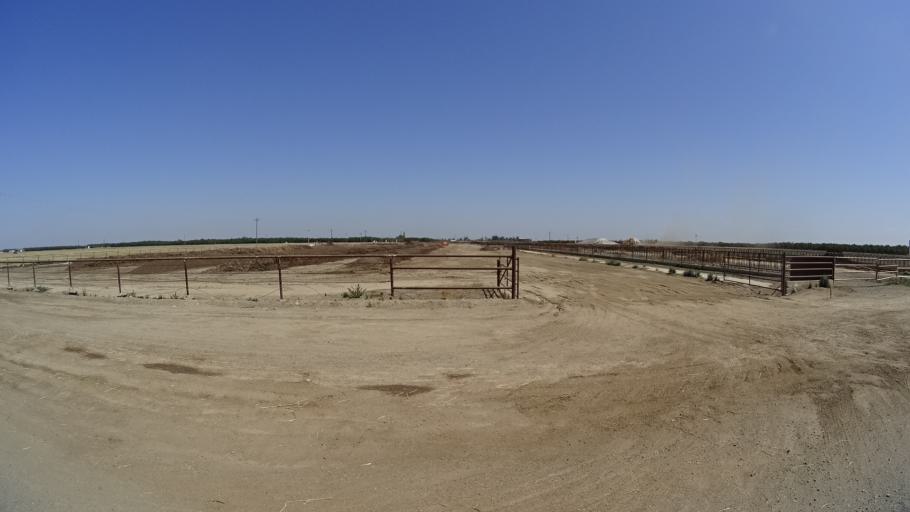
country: US
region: California
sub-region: Kings County
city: Lucerne
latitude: 36.3717
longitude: -119.6992
